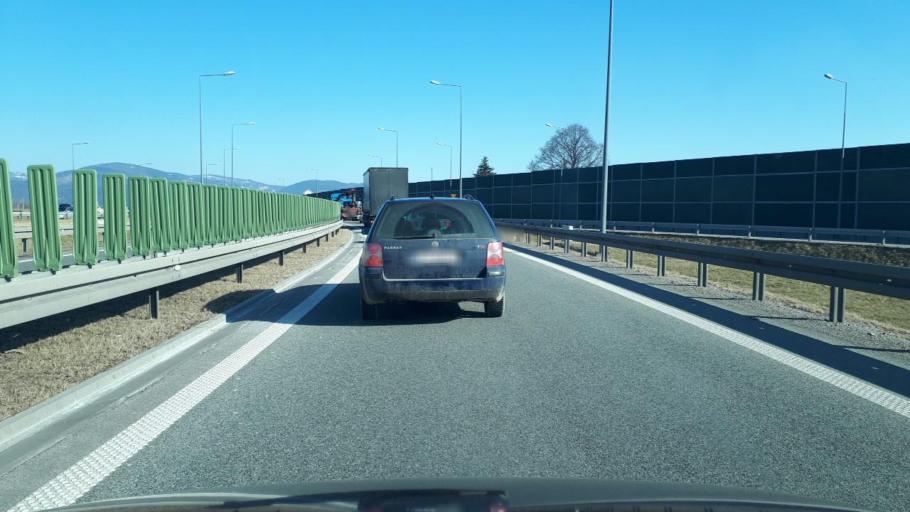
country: PL
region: Silesian Voivodeship
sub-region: Powiat zywiecki
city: Pietrzykowice
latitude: 49.6824
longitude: 19.1699
